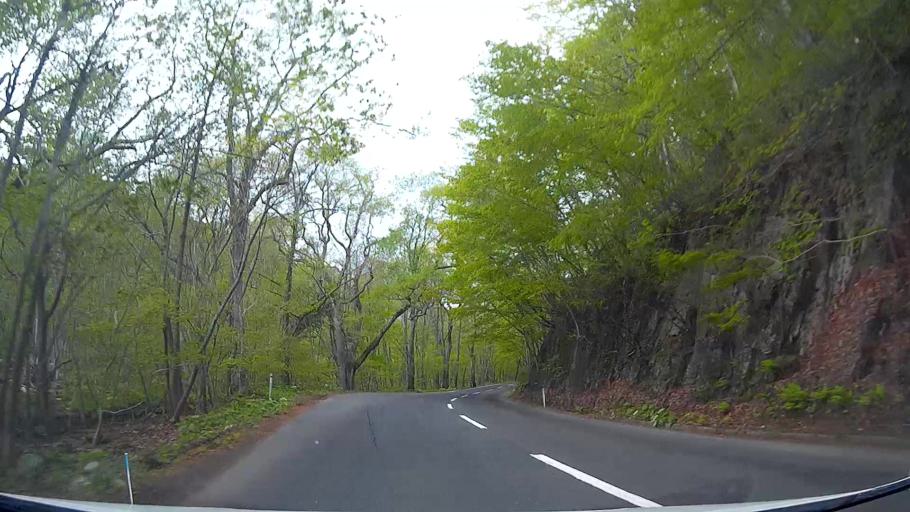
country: JP
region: Aomori
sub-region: Aomori Shi
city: Furudate
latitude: 40.5712
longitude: 140.9789
